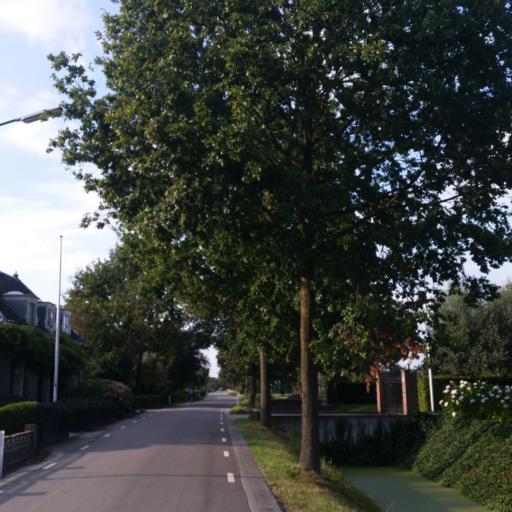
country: NL
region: Utrecht
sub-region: Gemeente IJsselstein
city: IJsselstein
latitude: 52.0327
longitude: 5.0247
